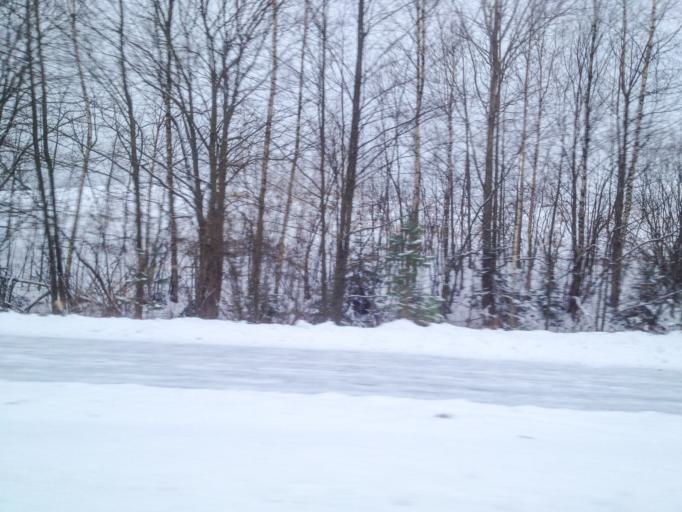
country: FI
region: Uusimaa
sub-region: Helsinki
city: Vantaa
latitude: 60.2098
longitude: 25.1738
